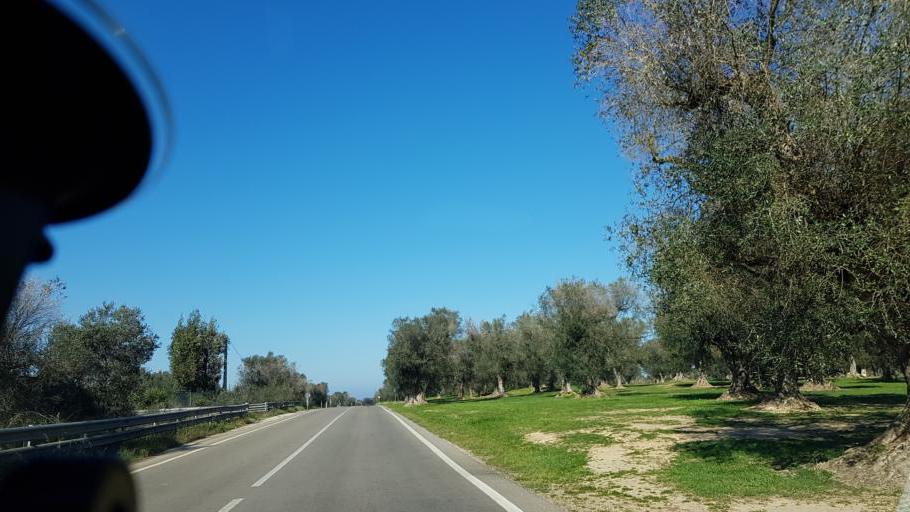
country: IT
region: Apulia
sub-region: Provincia di Brindisi
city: Torchiarolo
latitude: 40.5019
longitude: 18.0739
